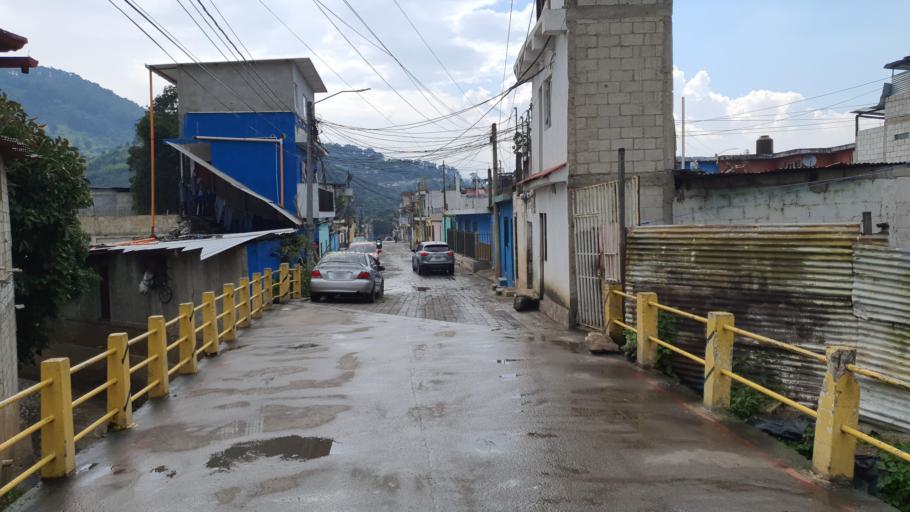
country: GT
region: Guatemala
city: Villa Canales
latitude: 14.4853
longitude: -90.5322
